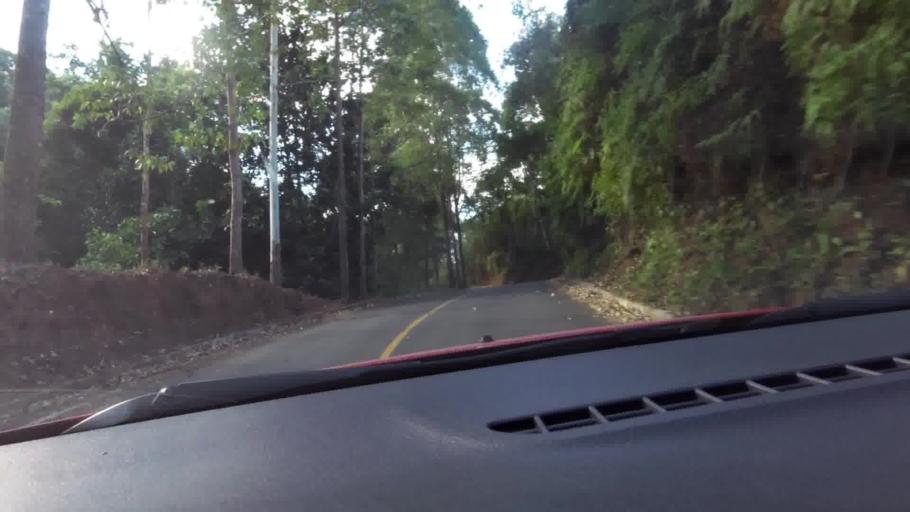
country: BR
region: Espirito Santo
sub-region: Guarapari
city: Guarapari
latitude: -20.5861
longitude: -40.5663
